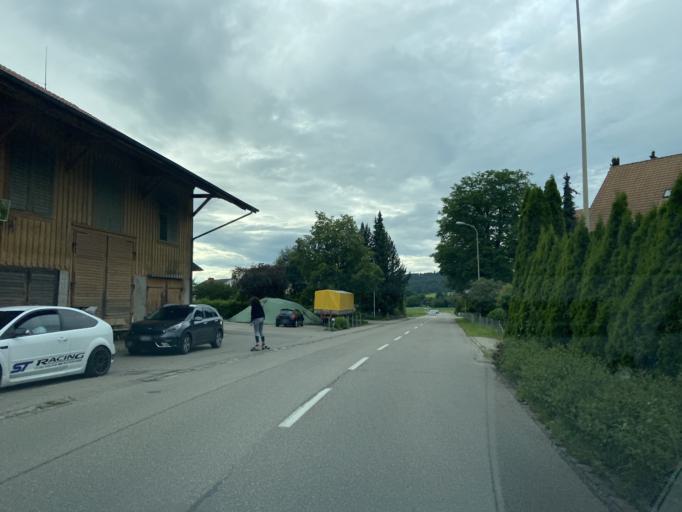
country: CH
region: Zurich
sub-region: Bezirk Winterthur
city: Elgg / Staedtchen und Umgebung
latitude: 47.4926
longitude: 8.8638
